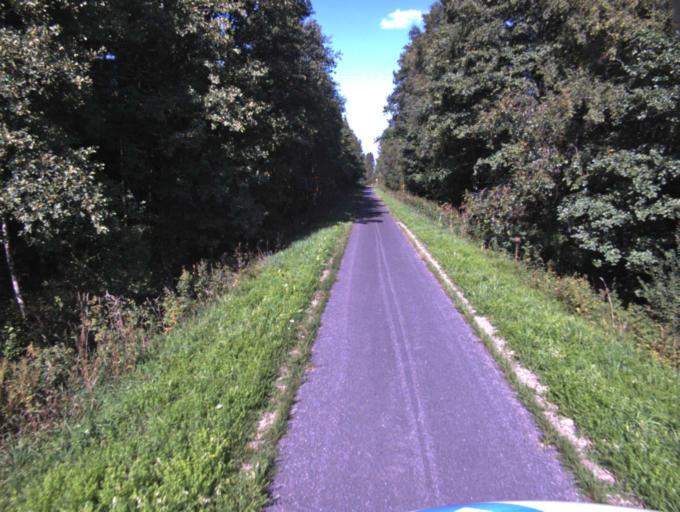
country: SE
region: Vaestra Goetaland
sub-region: Ulricehamns Kommun
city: Ulricehamn
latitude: 57.8108
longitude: 13.3550
